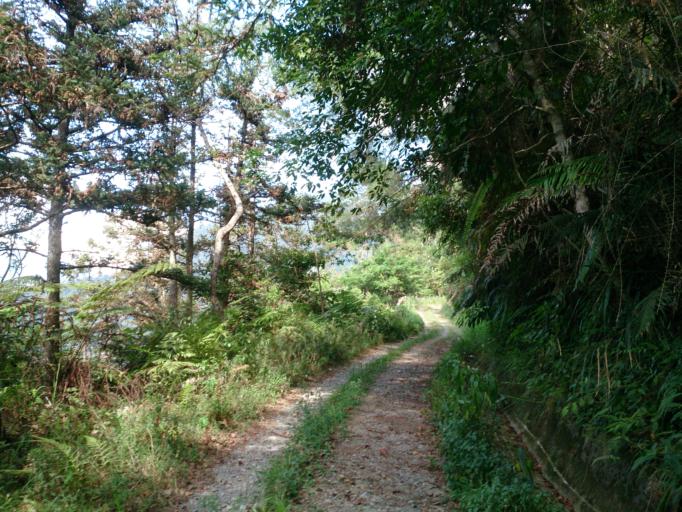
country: TW
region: Taiwan
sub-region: Nantou
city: Puli
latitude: 24.0837
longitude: 121.0280
